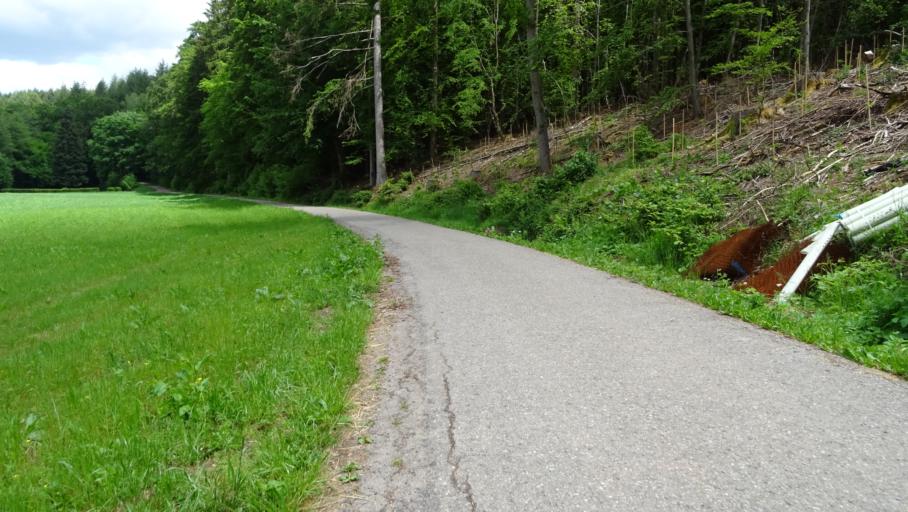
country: DE
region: Baden-Wuerttemberg
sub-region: Karlsruhe Region
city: Fahrenbach
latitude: 49.3943
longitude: 9.1760
